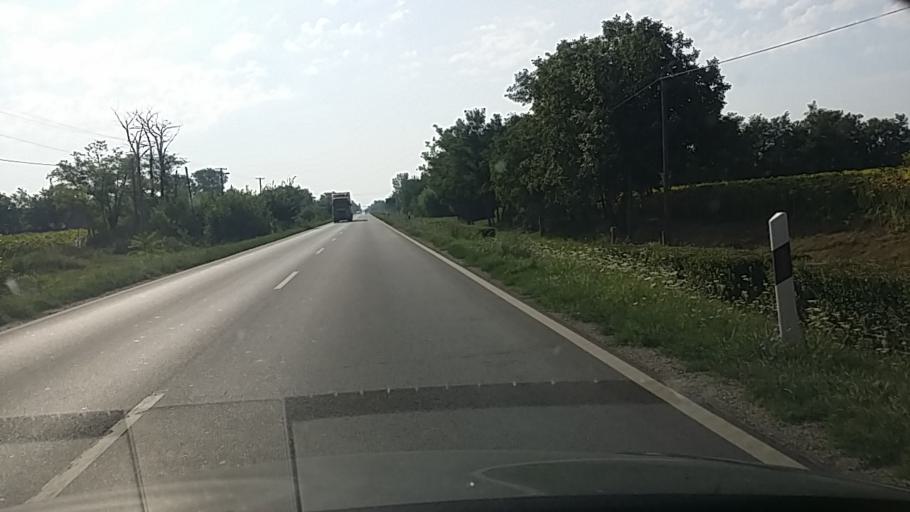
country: HU
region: Bekes
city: Kondoros
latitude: 46.8036
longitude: 20.7064
